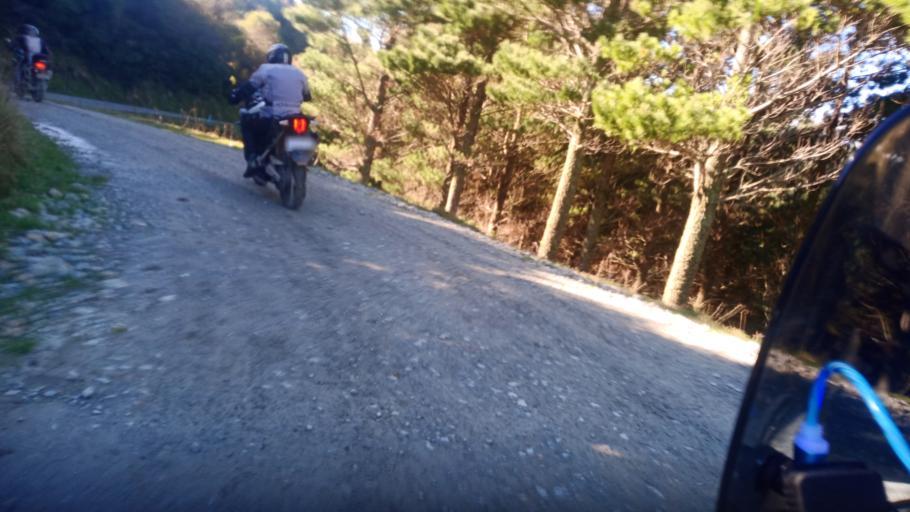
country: NZ
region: Hawke's Bay
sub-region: Wairoa District
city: Wairoa
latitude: -38.6662
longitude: 177.4782
